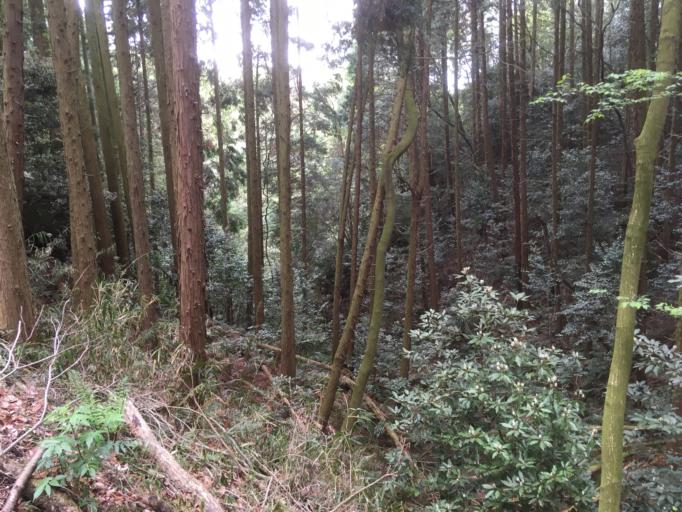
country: JP
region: Nara
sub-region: Ikoma-shi
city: Ikoma
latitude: 34.6968
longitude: 135.6764
